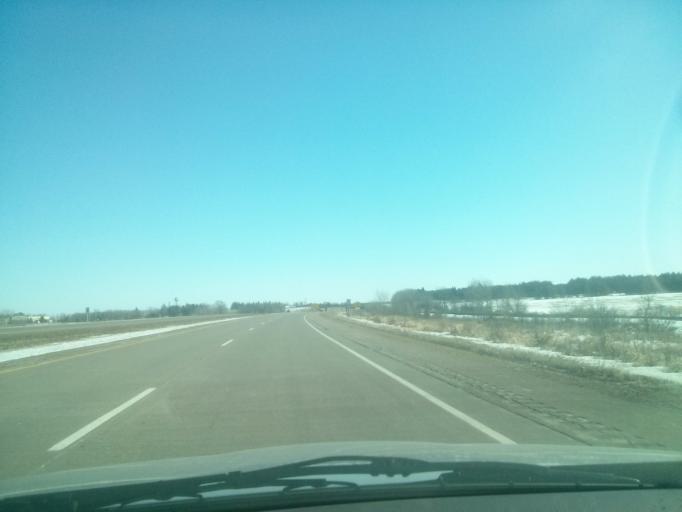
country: US
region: Wisconsin
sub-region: Saint Croix County
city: New Richmond
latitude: 45.1250
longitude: -92.5771
